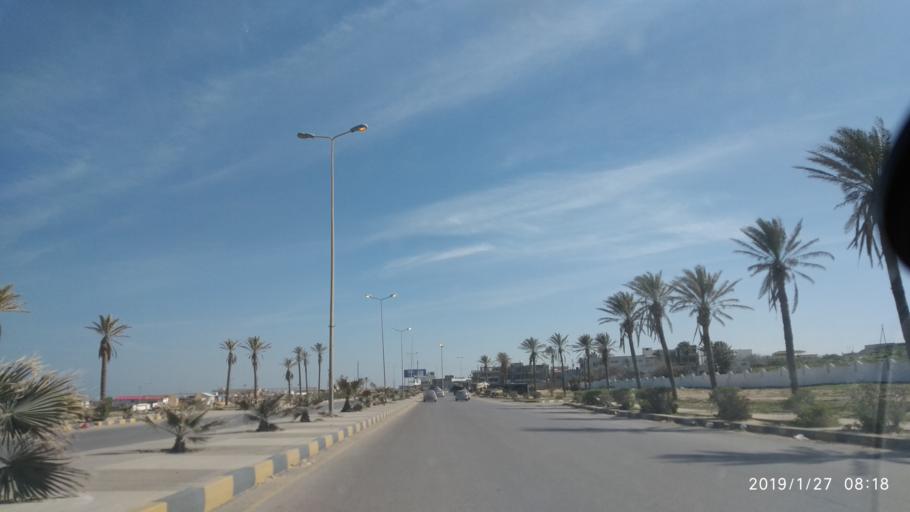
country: LY
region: Tripoli
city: Tagiura
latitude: 32.8947
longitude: 13.3402
